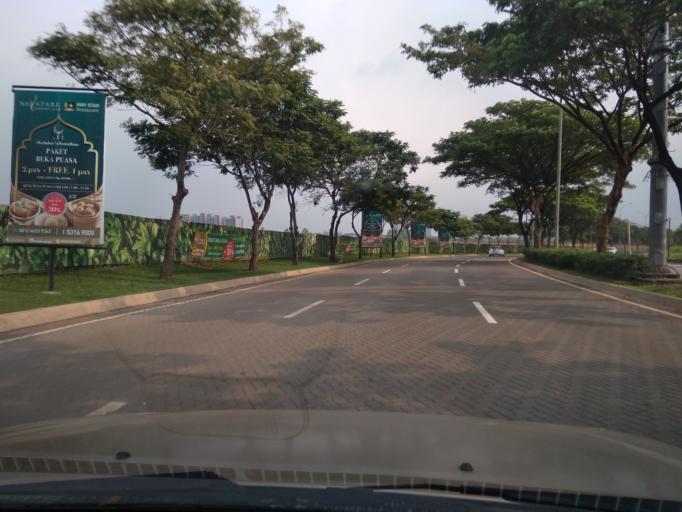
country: ID
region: West Java
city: Serpong
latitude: -6.2880
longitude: 106.6537
